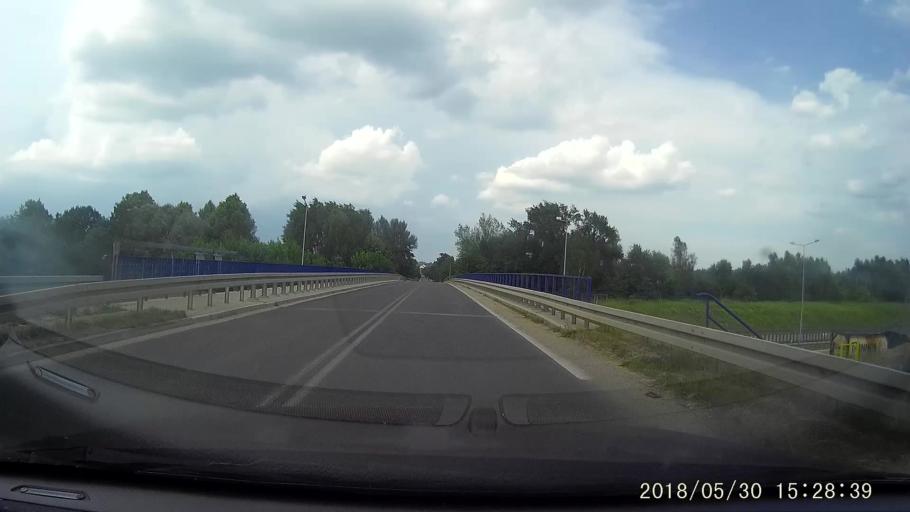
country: PL
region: Lower Silesian Voivodeship
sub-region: Powiat zgorzelecki
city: Zgorzelec
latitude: 51.1749
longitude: 15.0206
